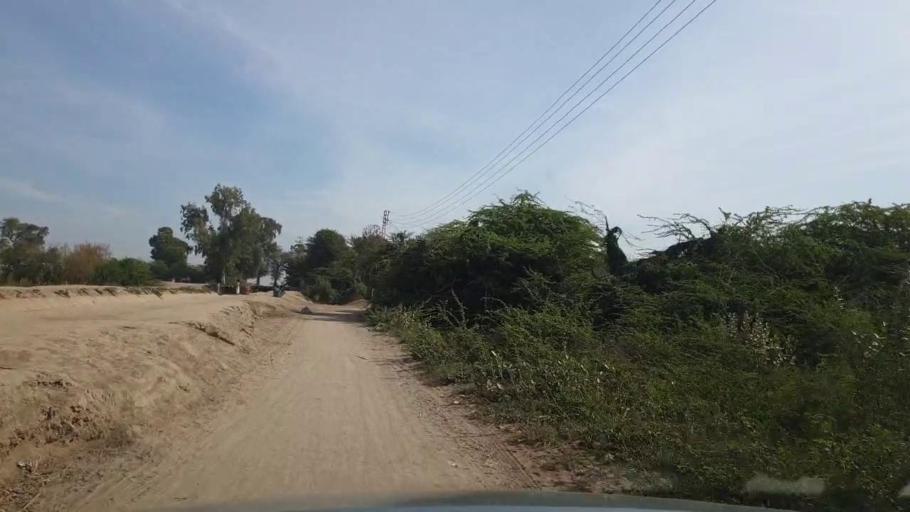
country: PK
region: Sindh
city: Kunri
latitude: 25.1738
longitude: 69.5764
